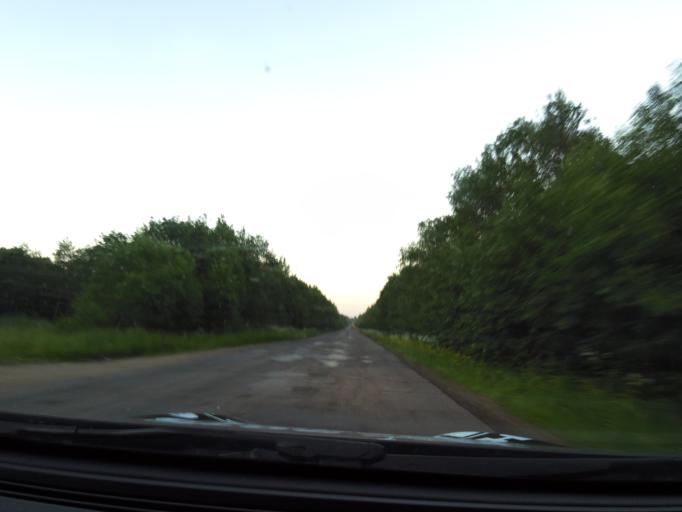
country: RU
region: Leningrad
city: Voznesen'ye
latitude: 60.8284
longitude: 35.7064
